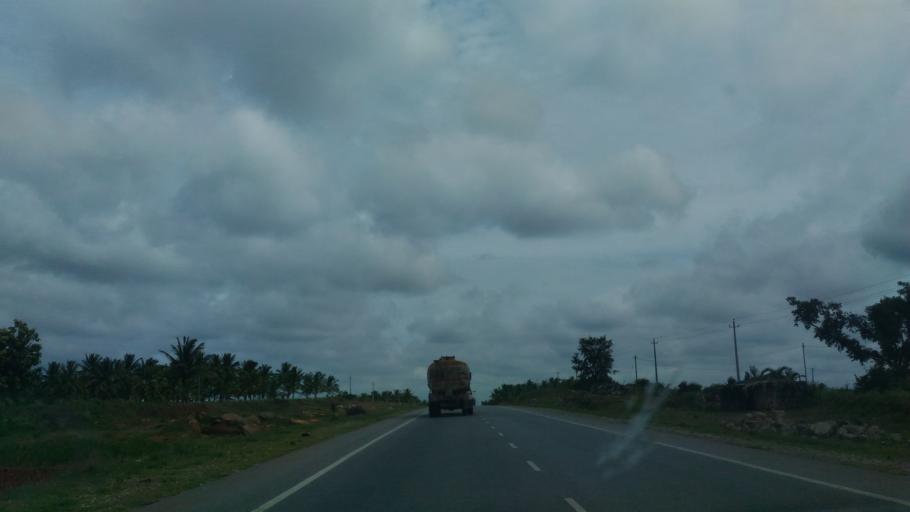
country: IN
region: Karnataka
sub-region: Hassan
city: Channarayapatna
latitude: 12.9115
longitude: 76.4188
